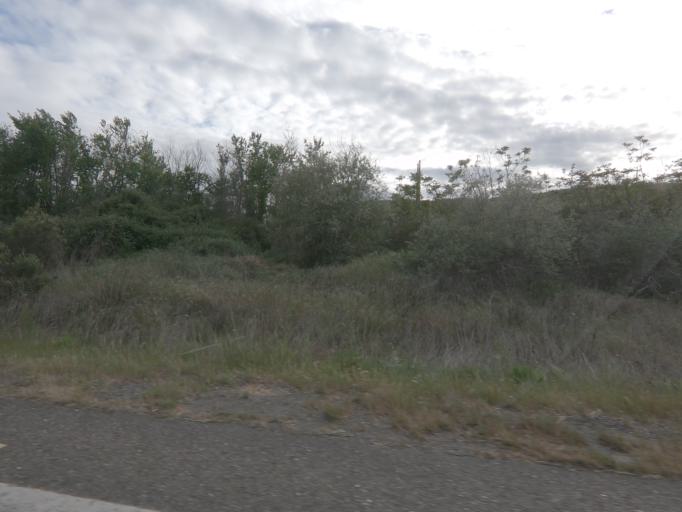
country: ES
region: Extremadura
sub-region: Provincia de Caceres
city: Coria
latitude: 39.9561
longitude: -6.5111
